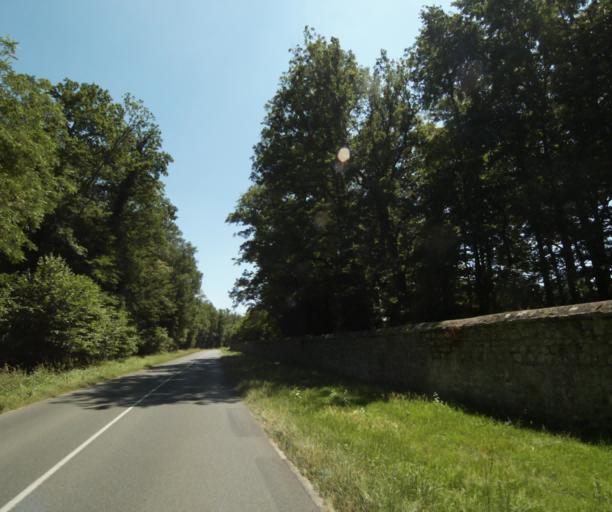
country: FR
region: Ile-de-France
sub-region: Departement de Seine-et-Marne
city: Noisy-sur-Ecole
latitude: 48.3823
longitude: 2.4983
